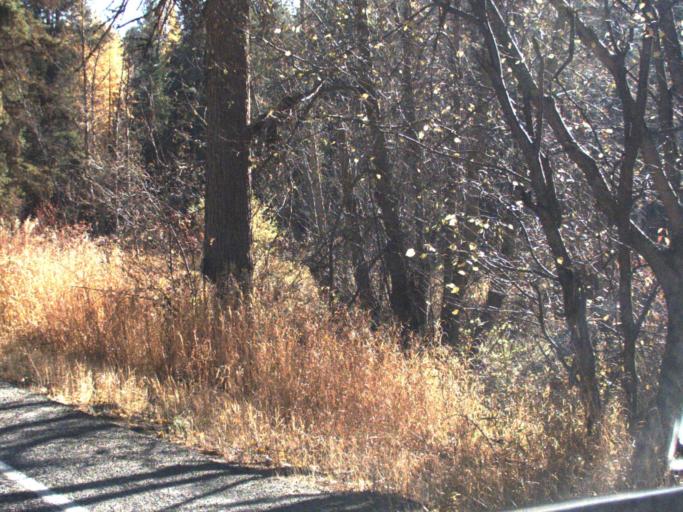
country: US
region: Washington
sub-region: Ferry County
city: Republic
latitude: 48.5976
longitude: -118.6460
